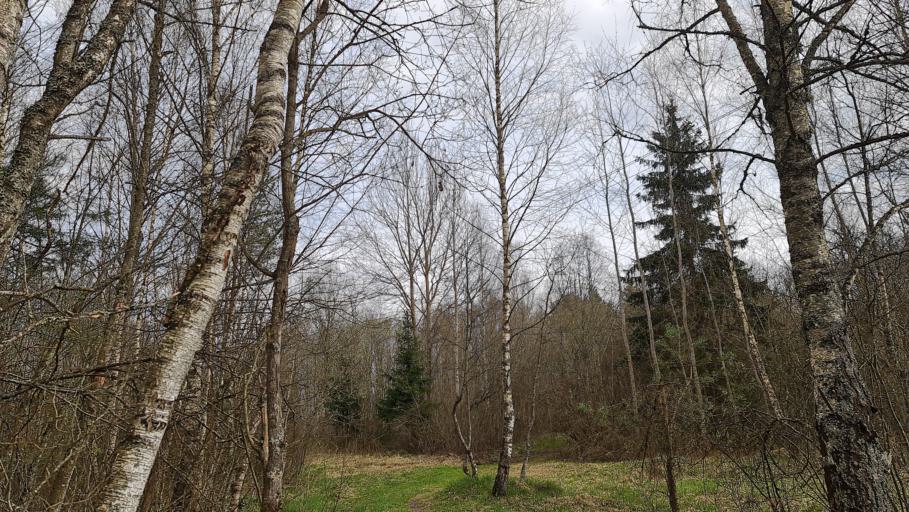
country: BY
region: Vitebsk
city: Byahoml'
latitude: 54.7492
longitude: 28.0534
